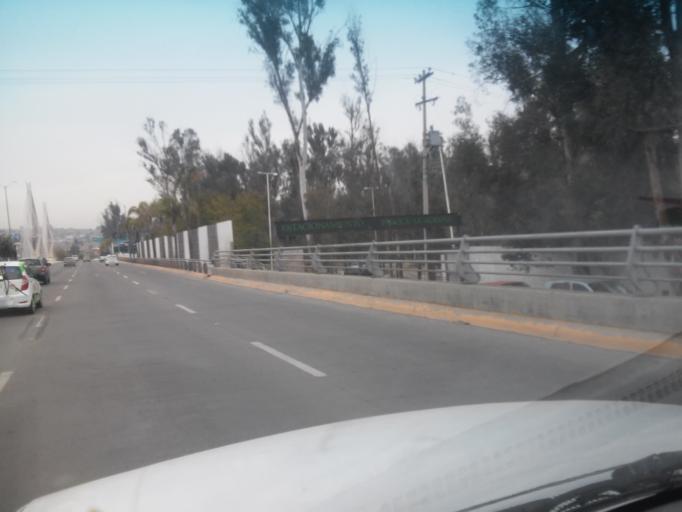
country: MX
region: Durango
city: Victoria de Durango
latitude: 24.0228
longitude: -104.6901
